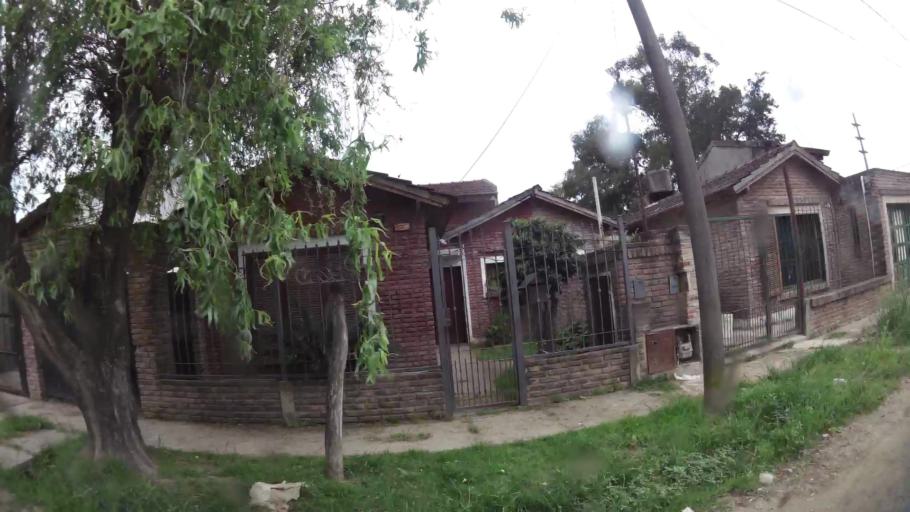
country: AR
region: Buenos Aires
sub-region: Partido de Zarate
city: Zarate
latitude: -34.1103
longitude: -59.0390
